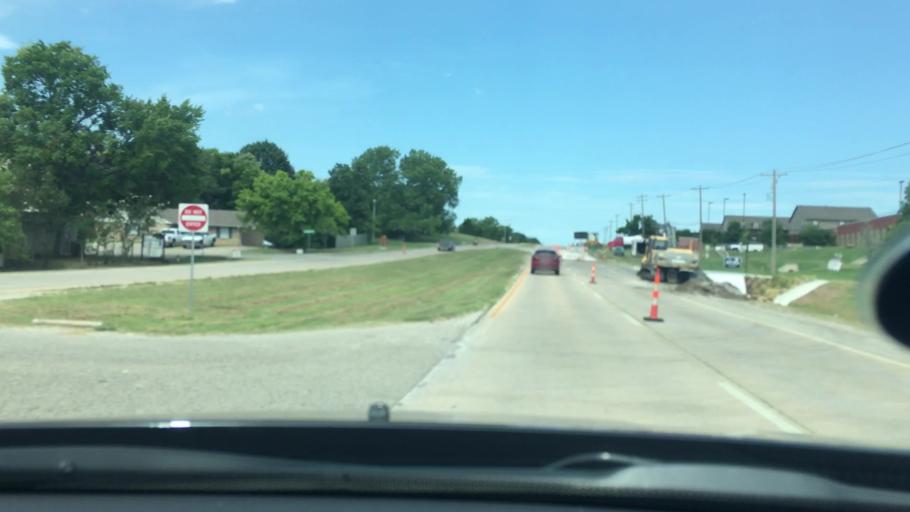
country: US
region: Oklahoma
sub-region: Pontotoc County
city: Ada
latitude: 34.7816
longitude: -96.6411
